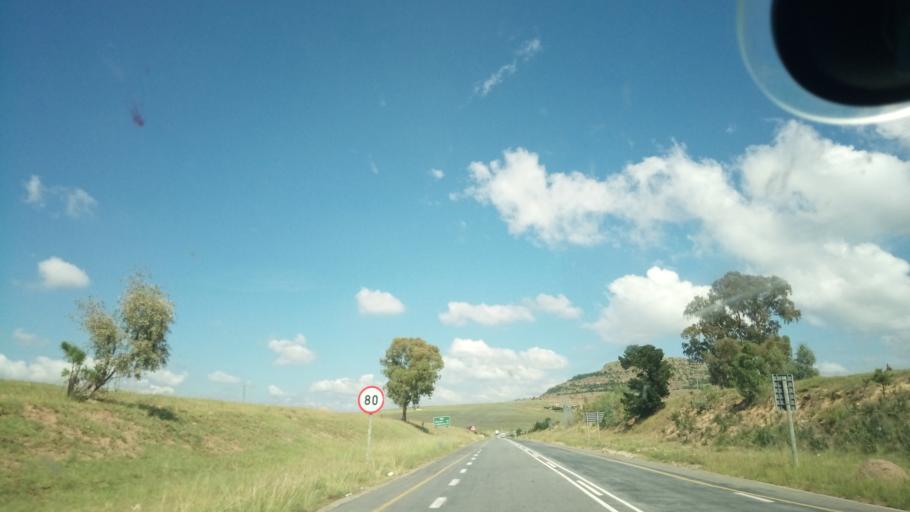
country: ZA
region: Orange Free State
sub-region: Thabo Mofutsanyana District Municipality
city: Ficksburg
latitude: -28.8912
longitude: 27.8548
